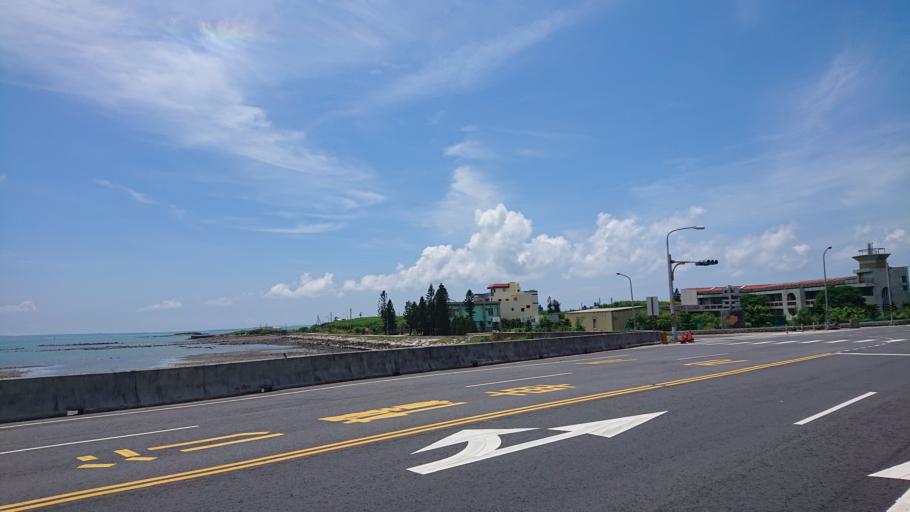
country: TW
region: Taiwan
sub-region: Penghu
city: Ma-kung
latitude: 23.6102
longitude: 119.6100
